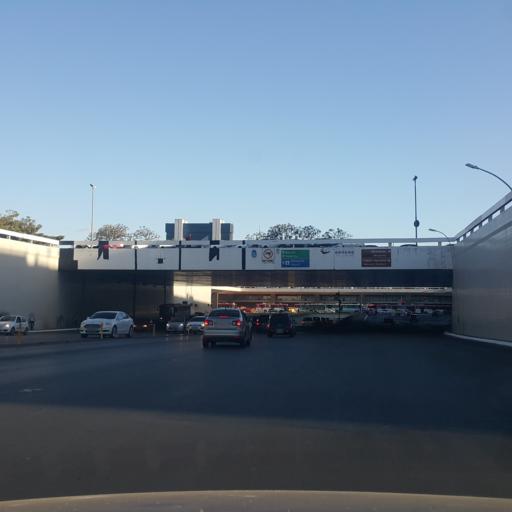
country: BR
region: Federal District
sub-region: Brasilia
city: Brasilia
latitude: -15.7908
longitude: -47.8818
